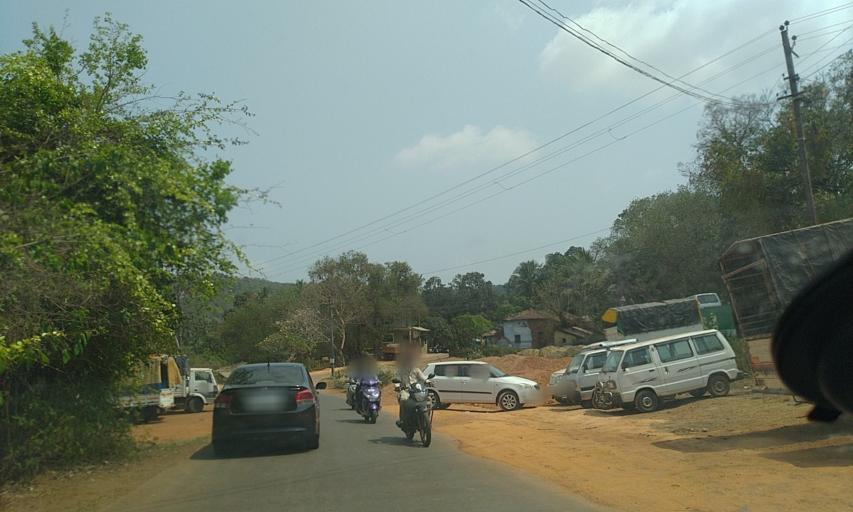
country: IN
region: Goa
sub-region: North Goa
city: Pernem
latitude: 15.7139
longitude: 73.7982
